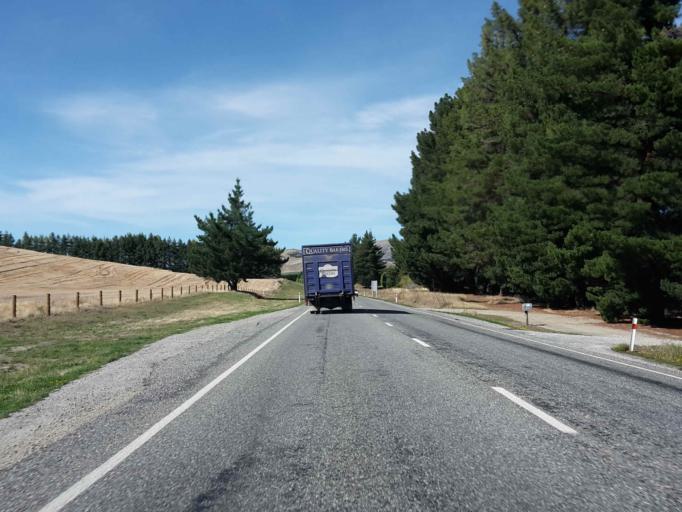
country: NZ
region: Otago
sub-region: Queenstown-Lakes District
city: Wanaka
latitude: -44.7106
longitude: 169.2074
